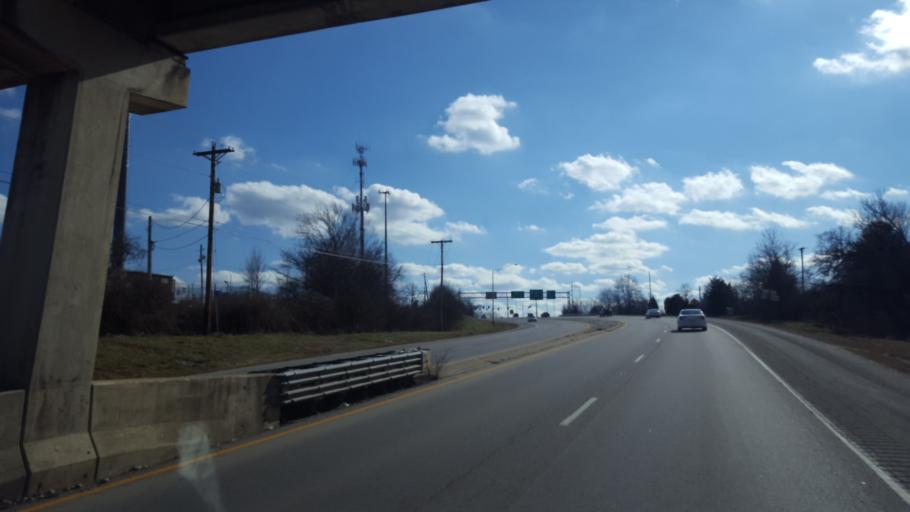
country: US
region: Kentucky
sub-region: Franklin County
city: Frankfort
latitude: 38.2090
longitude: -84.8371
